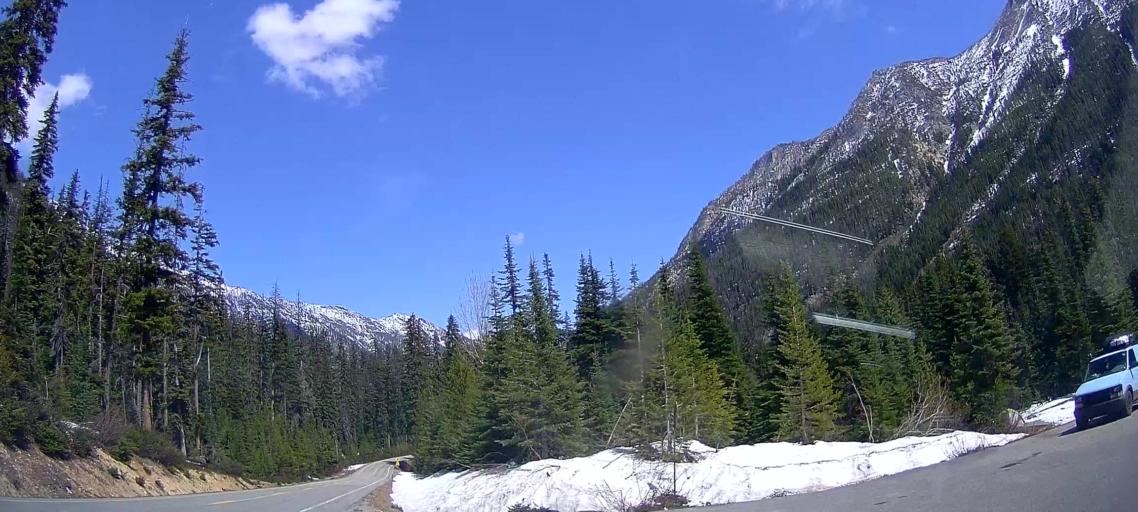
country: US
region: Washington
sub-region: Chelan County
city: Granite Falls
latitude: 48.5816
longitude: -120.6238
